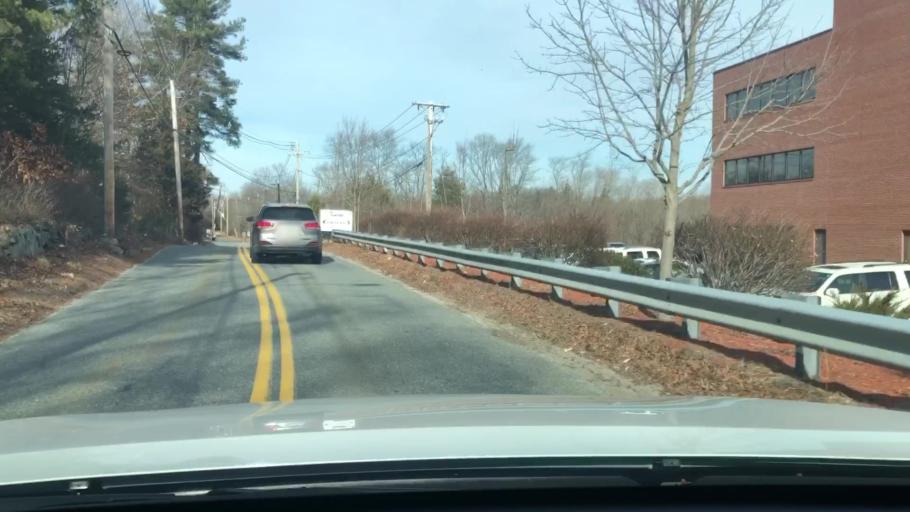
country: US
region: Massachusetts
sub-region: Worcester County
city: Milford
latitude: 42.1400
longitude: -71.4876
